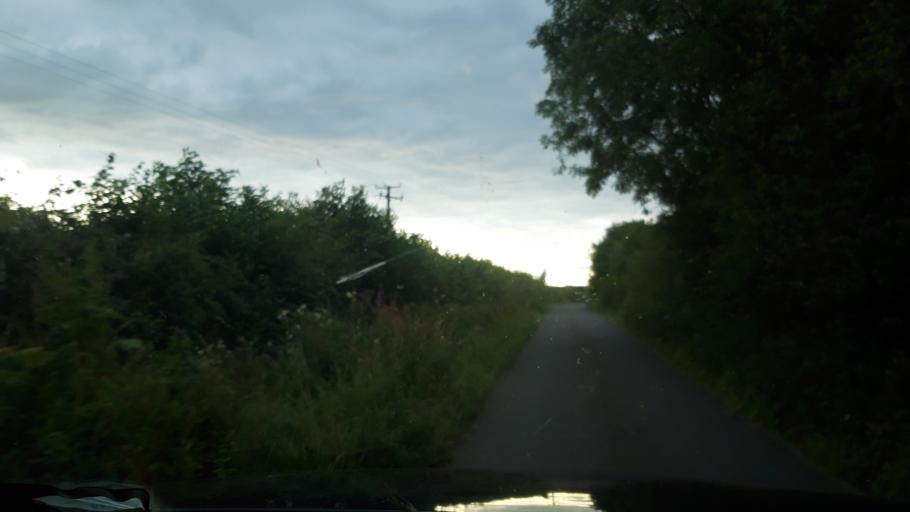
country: IE
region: Leinster
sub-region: Kilkenny
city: Graiguenamanagh
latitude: 52.5847
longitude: -6.9937
